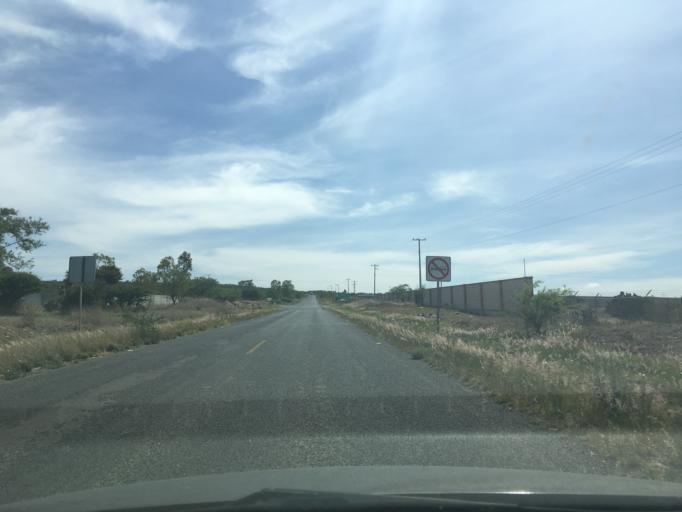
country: MX
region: Queretaro
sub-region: San Juan del Rio
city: El Jazmin
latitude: 20.3107
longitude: -100.0488
